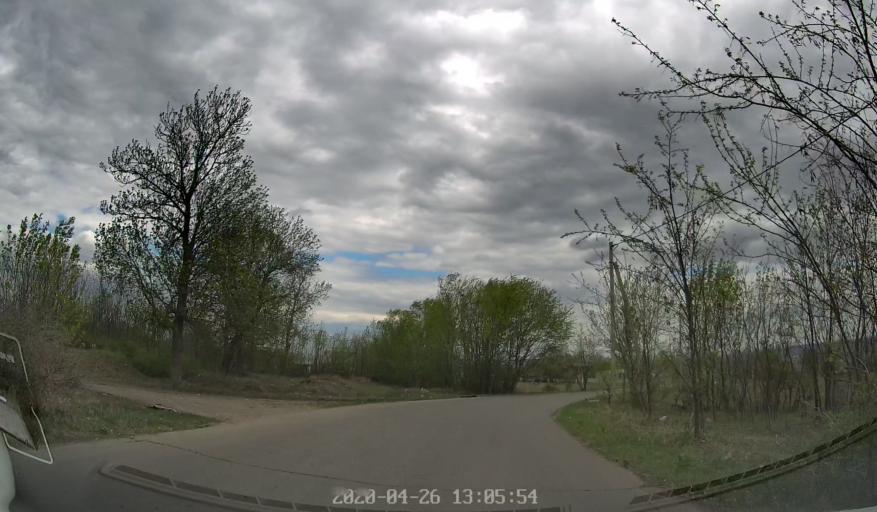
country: MD
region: Chisinau
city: Vadul lui Voda
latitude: 47.0796
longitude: 29.0677
